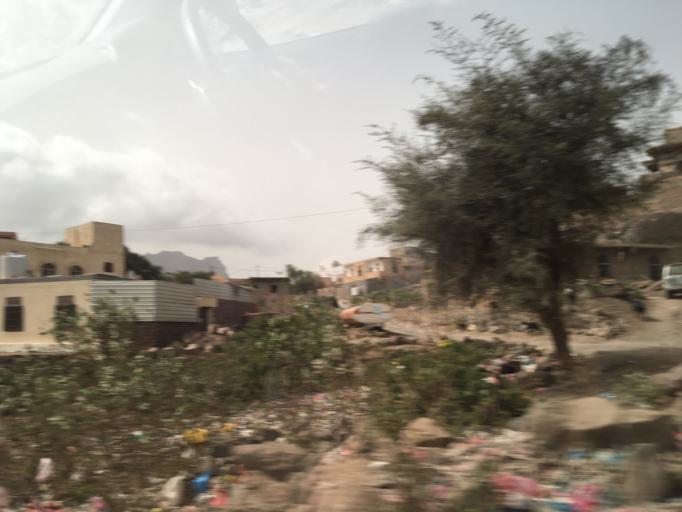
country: YE
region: Ad Dali'
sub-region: Ad Dhale'e
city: Dhalie
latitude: 13.6971
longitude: 44.7325
